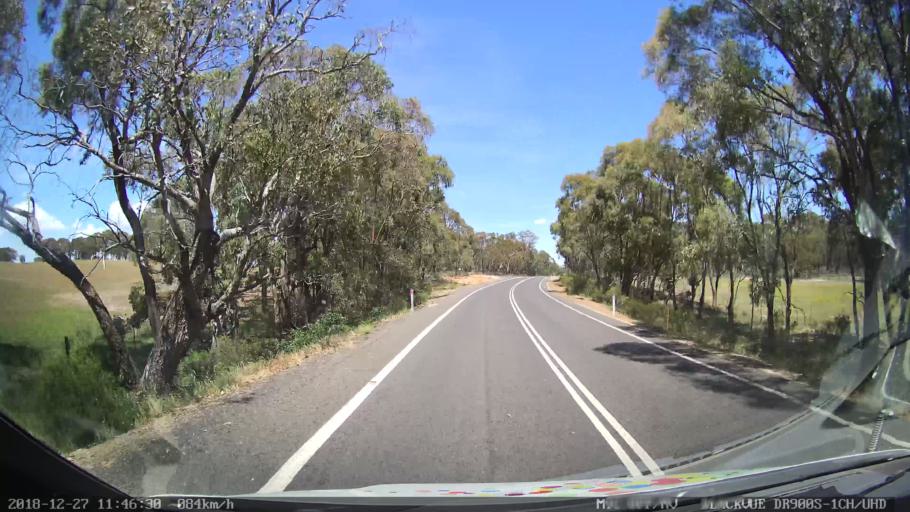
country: AU
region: New South Wales
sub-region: Bathurst Regional
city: Perthville
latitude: -33.5904
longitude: 149.4568
